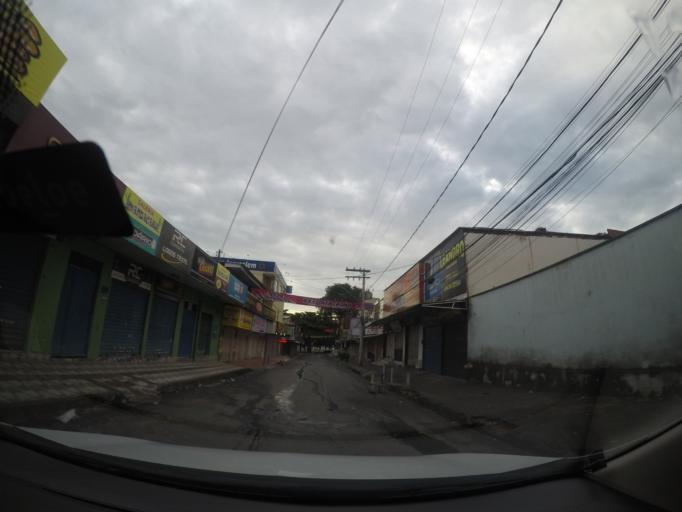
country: BR
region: Goias
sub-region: Goiania
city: Goiania
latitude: -16.6592
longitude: -49.2553
